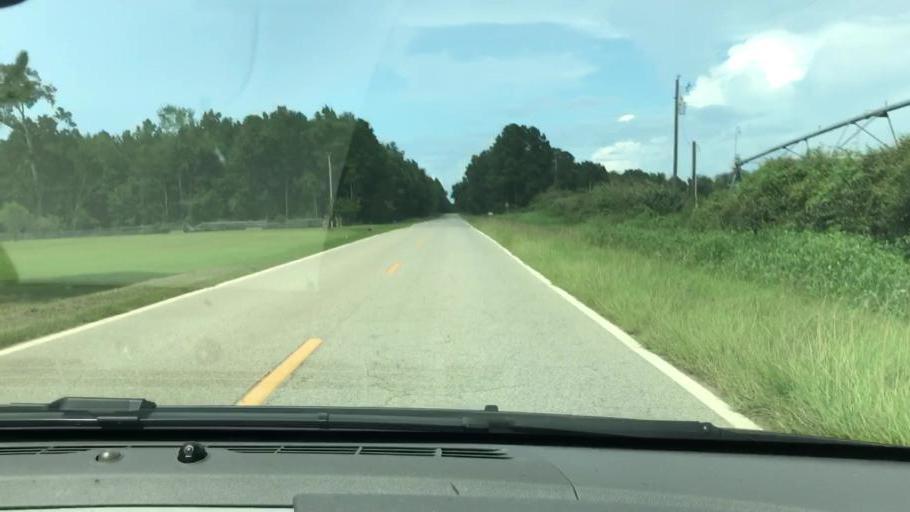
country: US
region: Georgia
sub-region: Seminole County
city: Donalsonville
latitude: 31.1457
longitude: -84.9949
